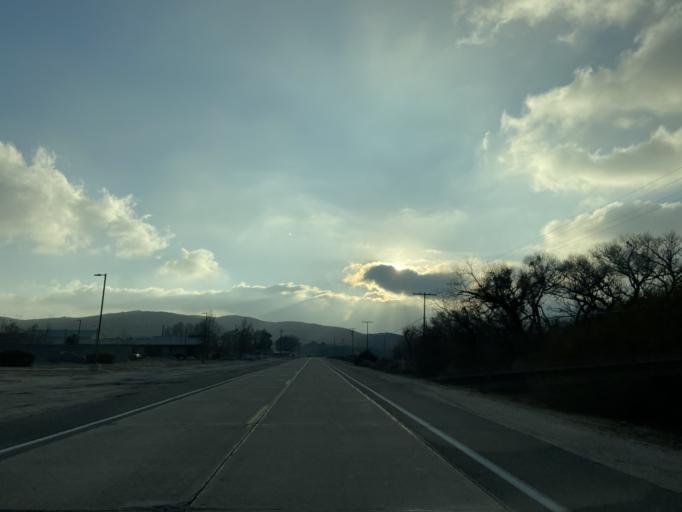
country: US
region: California
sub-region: San Diego County
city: Campo
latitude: 32.7211
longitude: -116.4478
